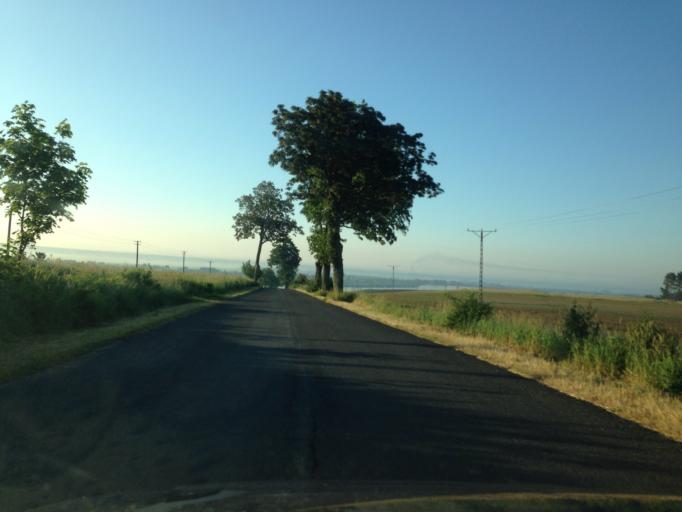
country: PL
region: Pomeranian Voivodeship
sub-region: Powiat tczewski
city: Gniew
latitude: 53.7832
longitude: 18.8234
